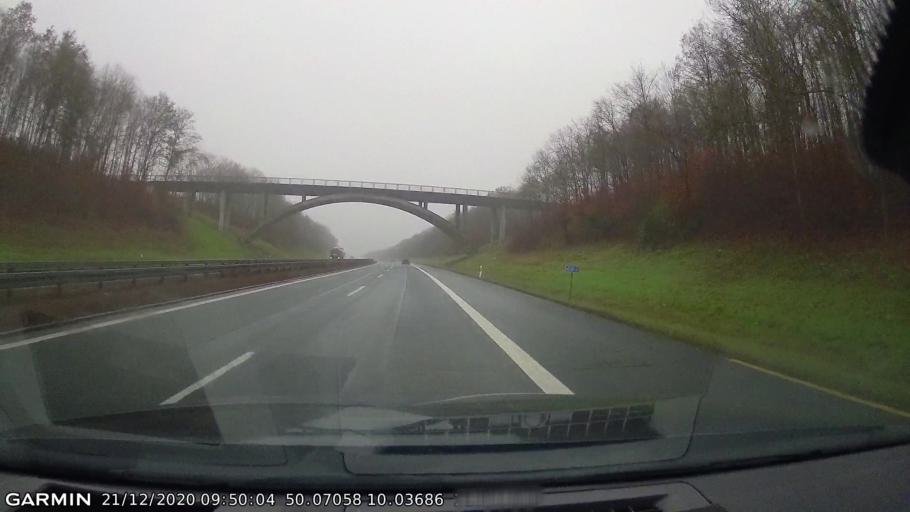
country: DE
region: Bavaria
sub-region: Regierungsbezirk Unterfranken
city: Wasserlosen
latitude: 50.0707
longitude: 10.0368
